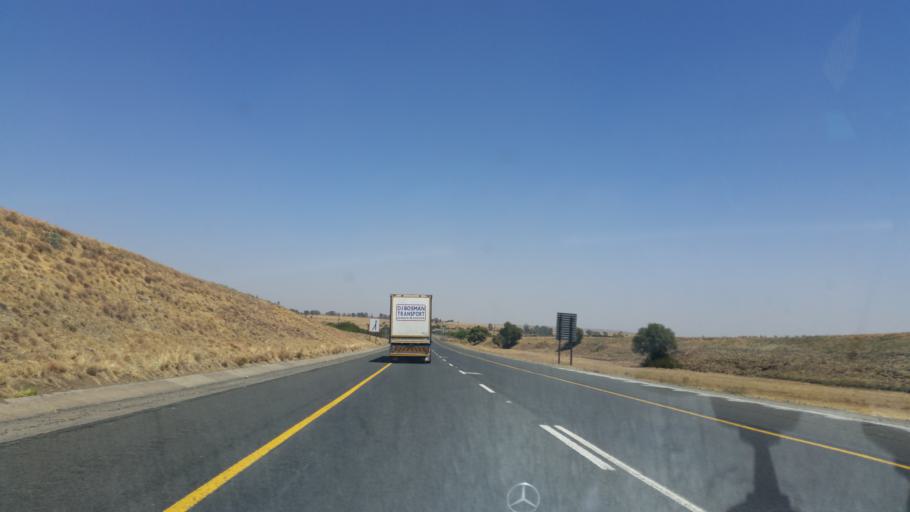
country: ZA
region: Orange Free State
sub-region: Lejweleputswa District Municipality
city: Winburg
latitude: -28.6276
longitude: 26.9096
